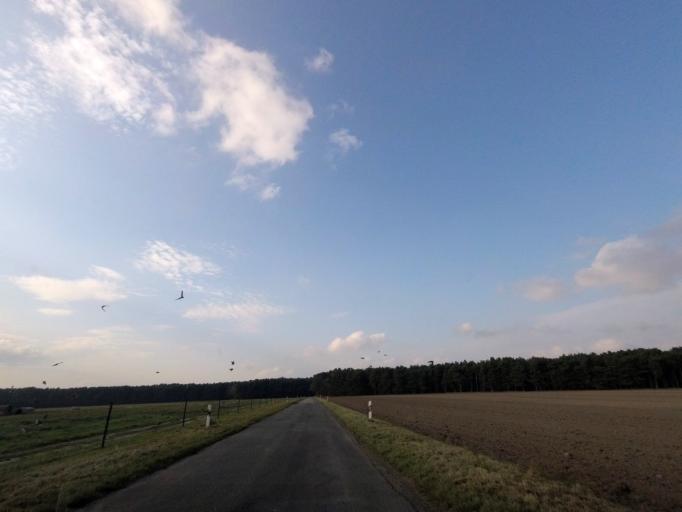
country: DE
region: Brandenburg
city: Bruck
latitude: 52.1560
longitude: 12.7155
